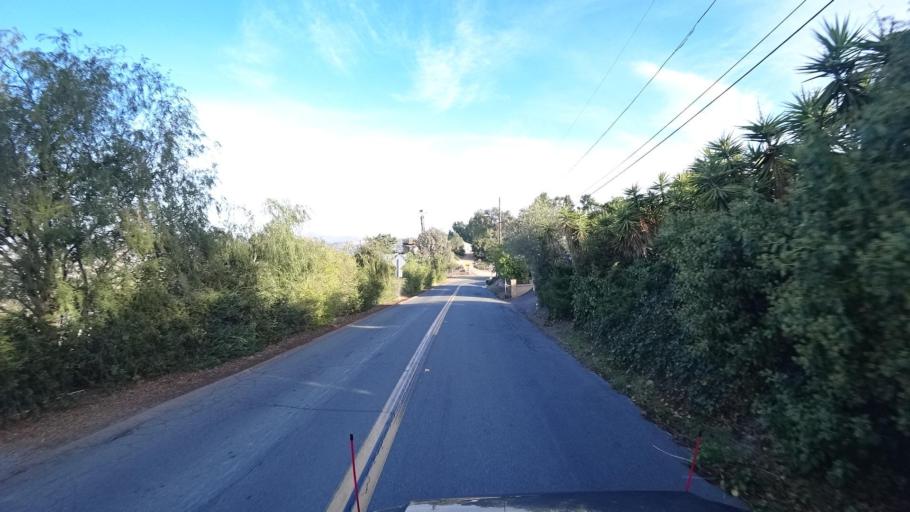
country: US
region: California
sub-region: San Diego County
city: Spring Valley
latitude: 32.7315
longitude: -116.9918
